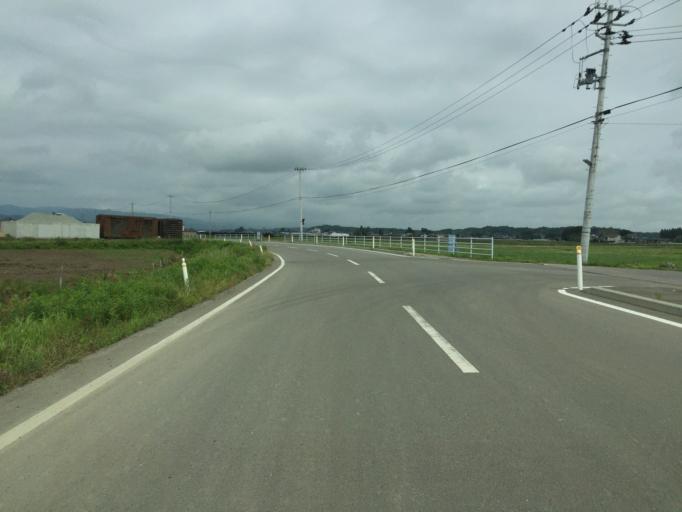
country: JP
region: Fukushima
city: Namie
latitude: 37.6968
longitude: 140.9908
